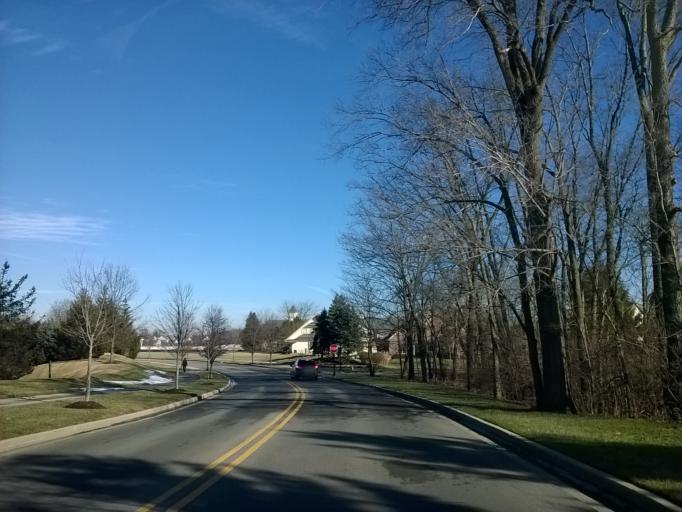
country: US
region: Indiana
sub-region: Boone County
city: Zionsville
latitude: 39.9756
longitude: -86.2442
